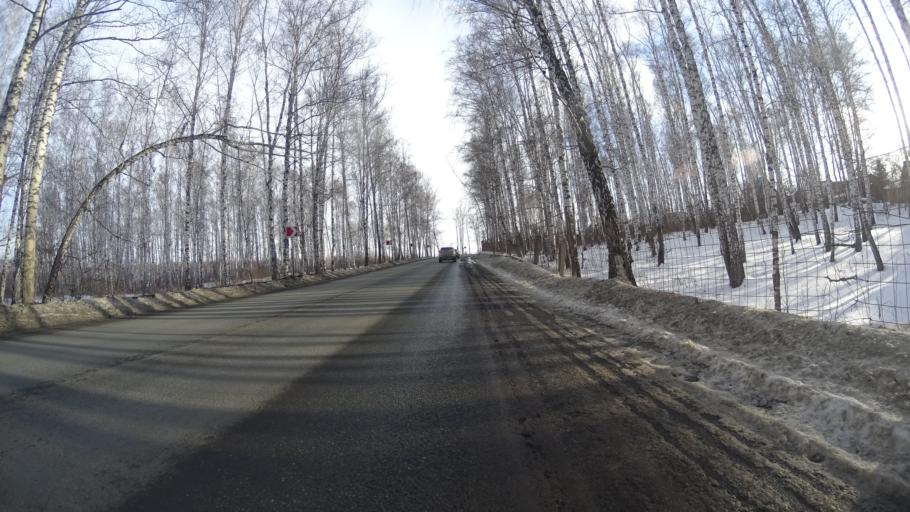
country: RU
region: Chelyabinsk
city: Sargazy
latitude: 55.1264
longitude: 61.2890
